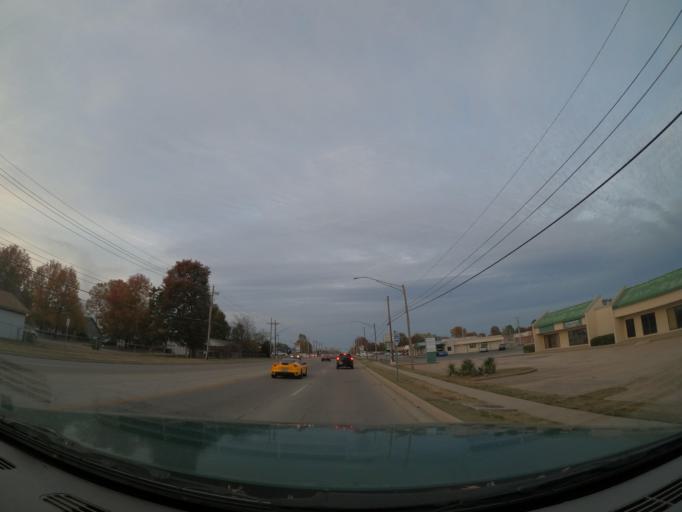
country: US
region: Oklahoma
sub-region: Tulsa County
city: Broken Arrow
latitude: 36.0296
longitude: -95.7974
